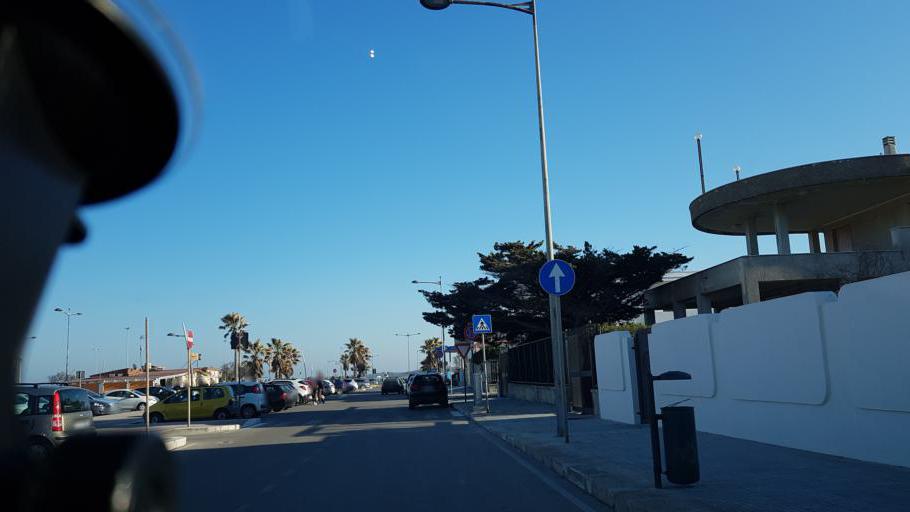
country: IT
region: Apulia
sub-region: Provincia di Lecce
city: Struda
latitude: 40.3913
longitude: 18.3051
